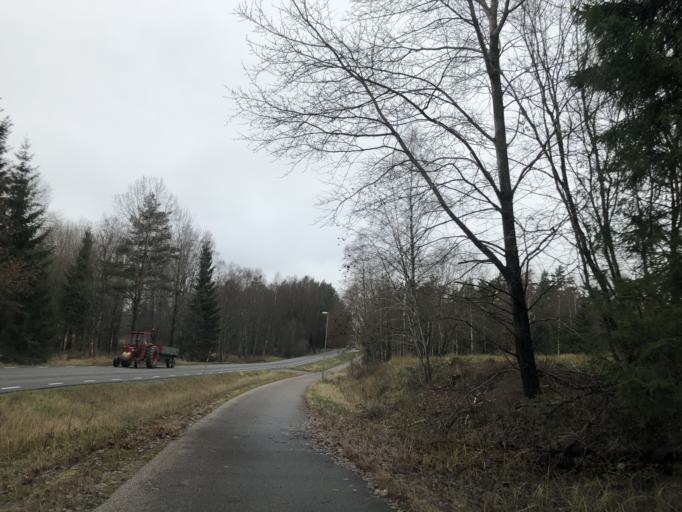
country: SE
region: Vaestra Goetaland
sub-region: Ulricehamns Kommun
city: Ulricehamn
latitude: 57.6701
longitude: 13.4437
